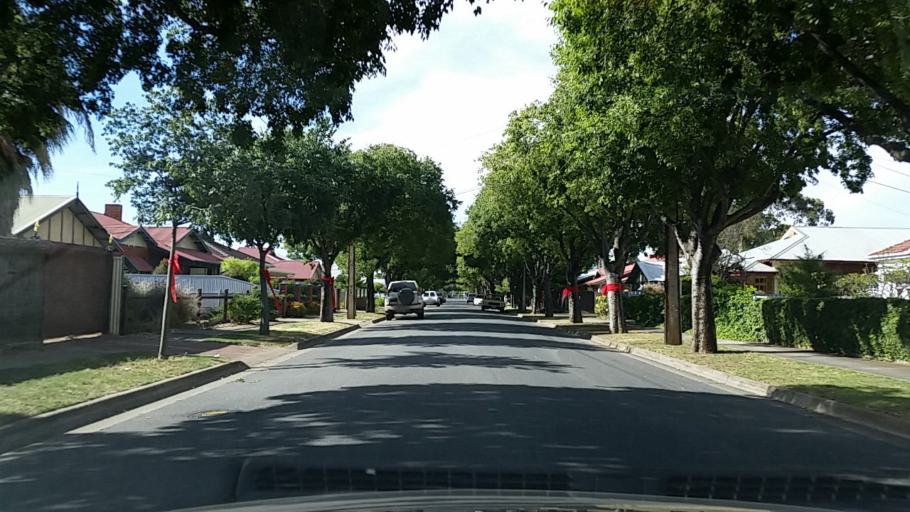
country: AU
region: South Australia
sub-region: Charles Sturt
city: Allenby Gardens
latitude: -34.9003
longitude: 138.5530
